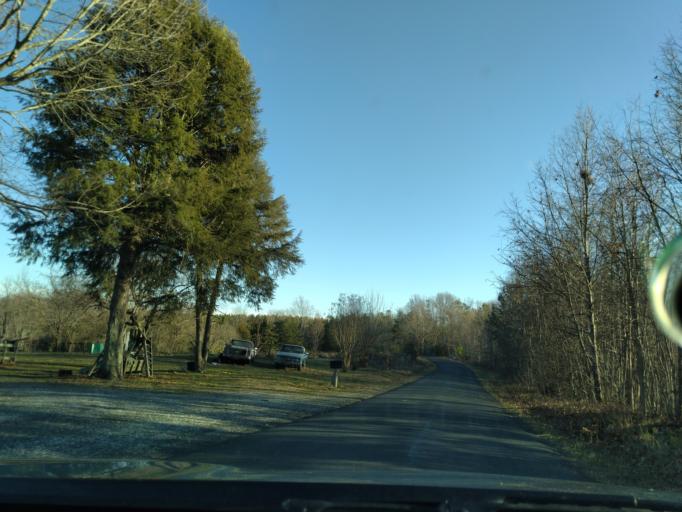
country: US
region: Virginia
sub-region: Buckingham County
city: Buckingham
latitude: 37.3675
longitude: -78.6158
